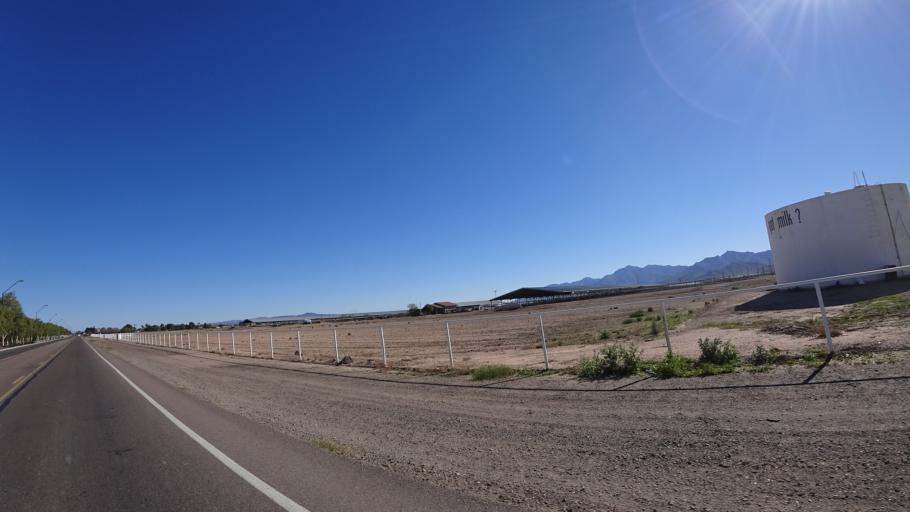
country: US
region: Arizona
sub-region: Maricopa County
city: Avondale
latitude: 33.4206
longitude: -112.3148
